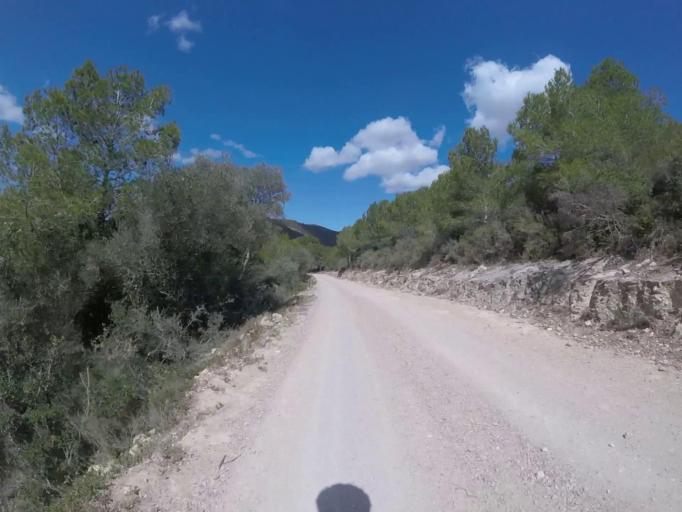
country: ES
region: Valencia
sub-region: Provincia de Castello
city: Santa Magdalena de Pulpis
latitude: 40.3250
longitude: 0.3410
